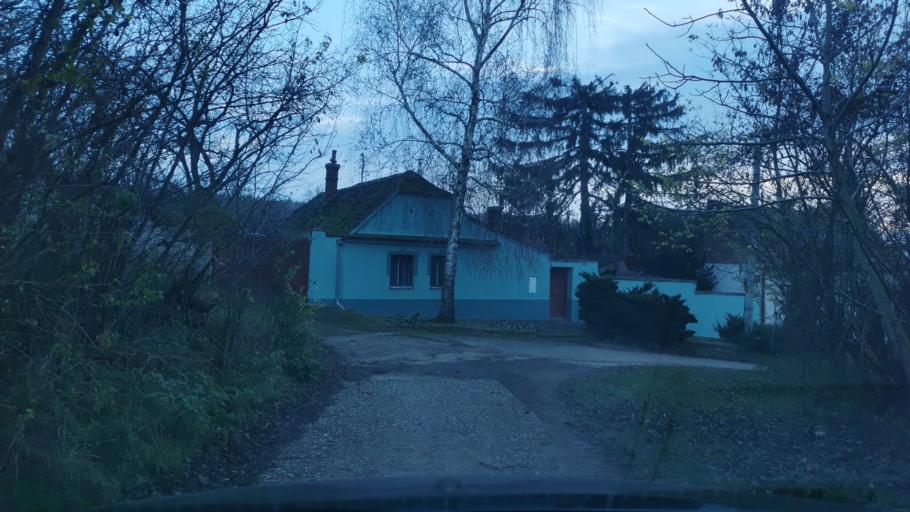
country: SK
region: Trnavsky
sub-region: Okres Skalica
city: Holic
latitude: 48.8032
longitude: 17.1683
